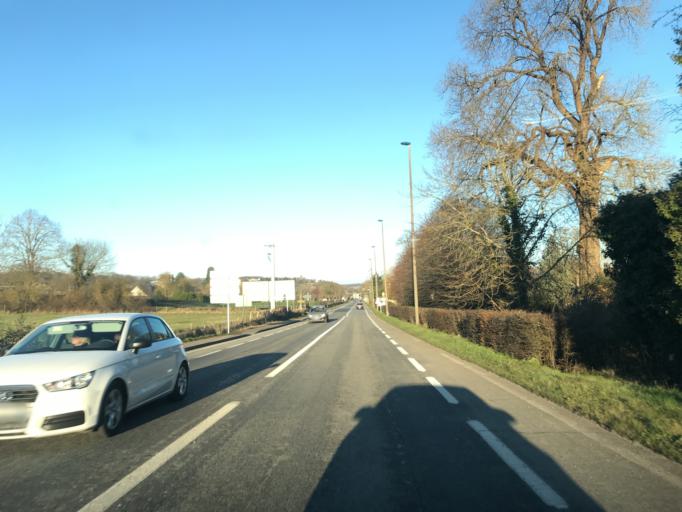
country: FR
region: Haute-Normandie
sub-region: Departement de l'Eure
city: Arnieres-sur-Iton
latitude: 49.0151
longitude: 1.1087
